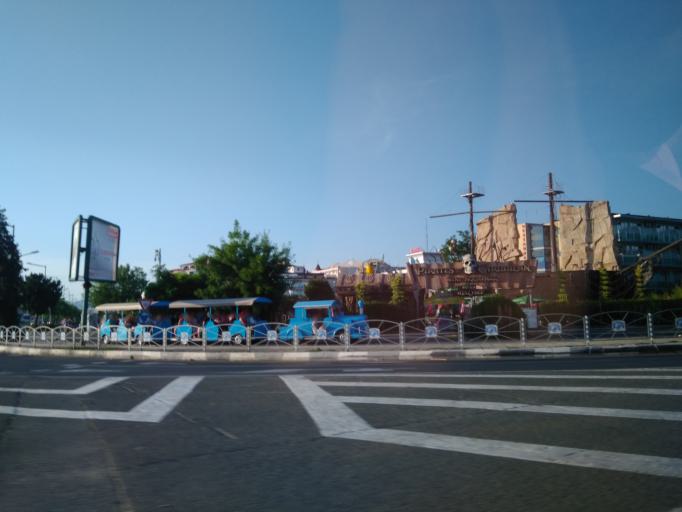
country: BG
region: Burgas
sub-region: Obshtina Nesebur
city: Nesebar
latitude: 42.6655
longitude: 27.7071
